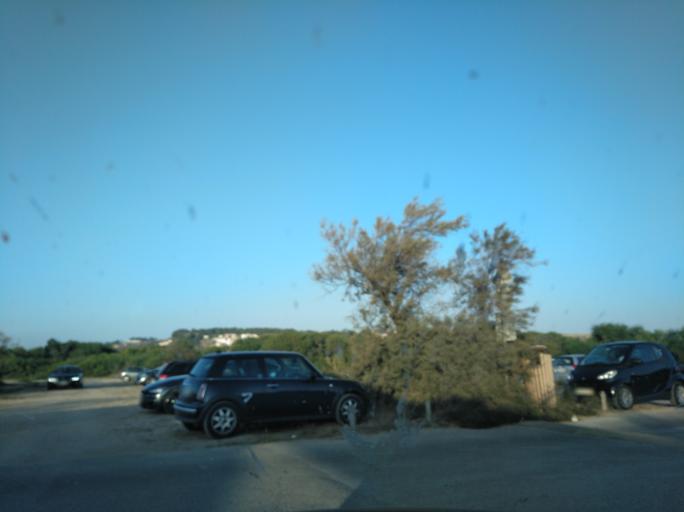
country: PT
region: Setubal
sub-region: Almada
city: Trafaria
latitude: 38.6613
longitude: -9.2546
